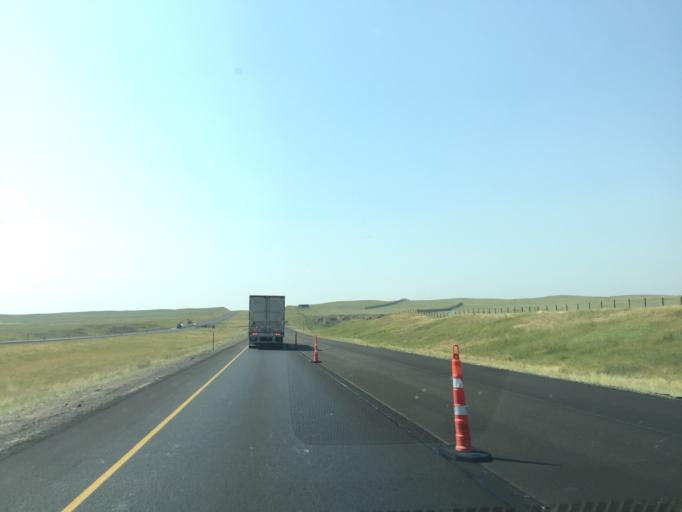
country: US
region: Wyoming
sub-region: Laramie County
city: Ranchettes
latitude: 41.3278
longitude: -104.8631
